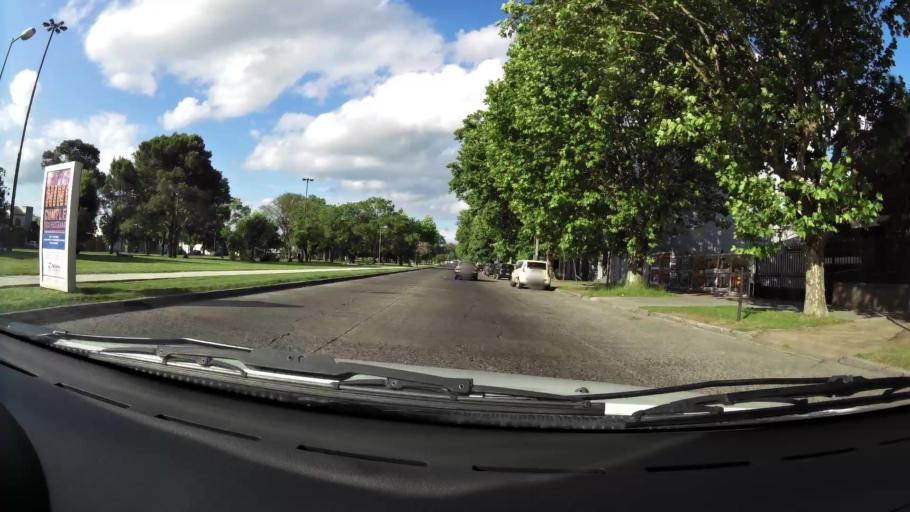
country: AR
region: Buenos Aires
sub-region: Partido de La Plata
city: La Plata
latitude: -34.8985
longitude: -57.9666
